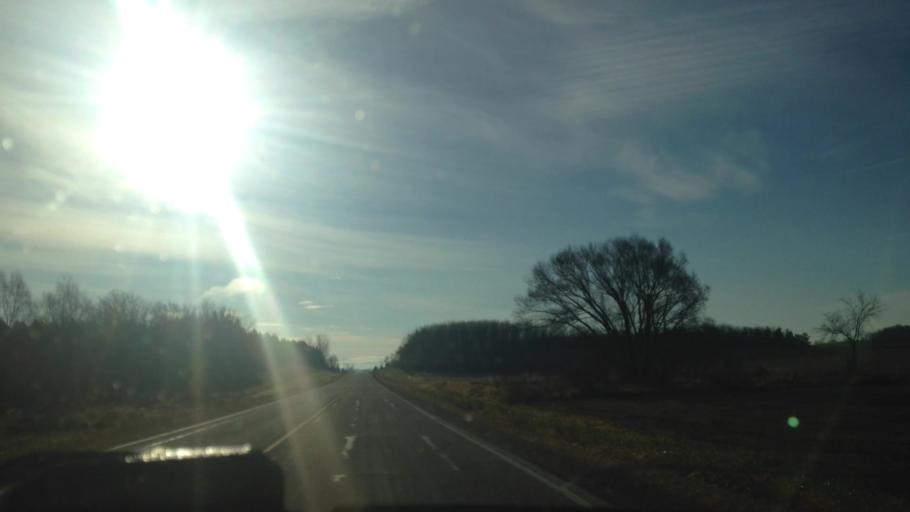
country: US
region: Wisconsin
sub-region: Dodge County
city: Mayville
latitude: 43.4917
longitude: -88.5198
